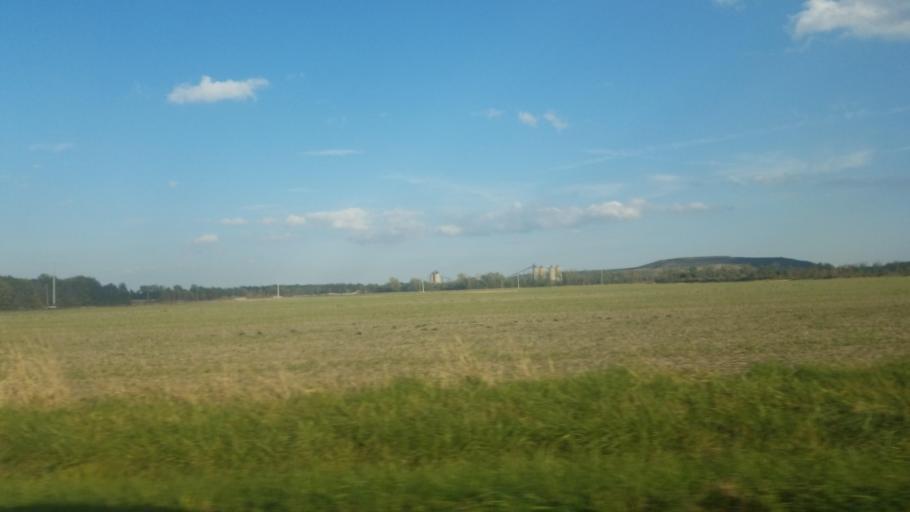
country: US
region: Illinois
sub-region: Saline County
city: Harrisburg
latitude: 37.8250
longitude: -88.6147
